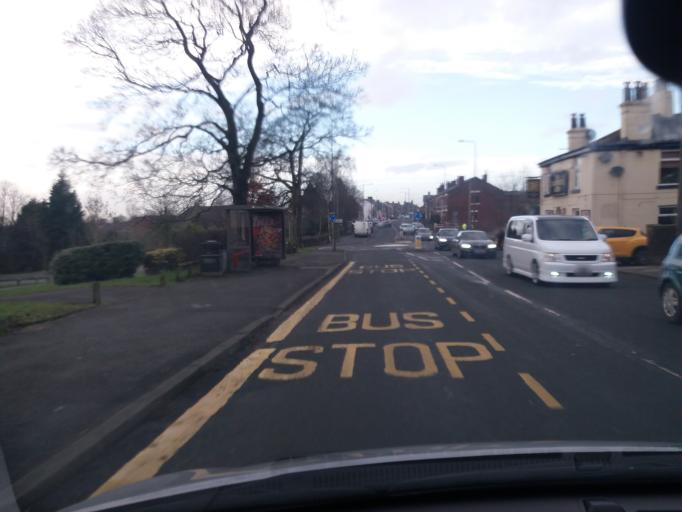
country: GB
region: England
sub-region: Lancashire
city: Adlington
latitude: 53.6211
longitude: -2.6033
